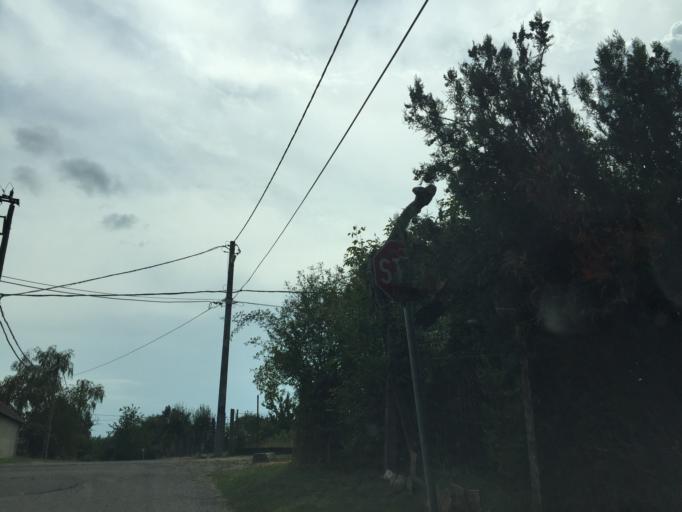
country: HU
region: Nograd
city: Nagyoroszi
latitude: 47.9746
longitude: 19.0998
